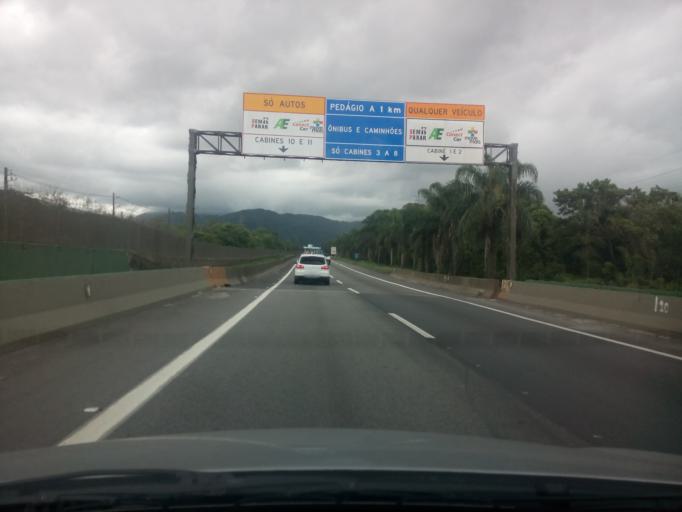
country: BR
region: Sao Paulo
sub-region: Santos
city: Santos
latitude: -23.9020
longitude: -46.2979
